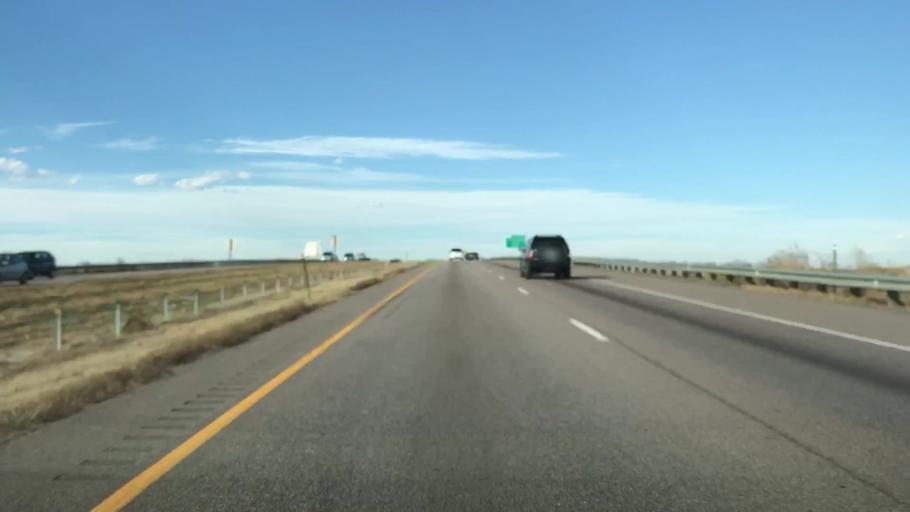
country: US
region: Colorado
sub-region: Larimer County
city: Loveland
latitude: 40.4199
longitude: -104.9925
